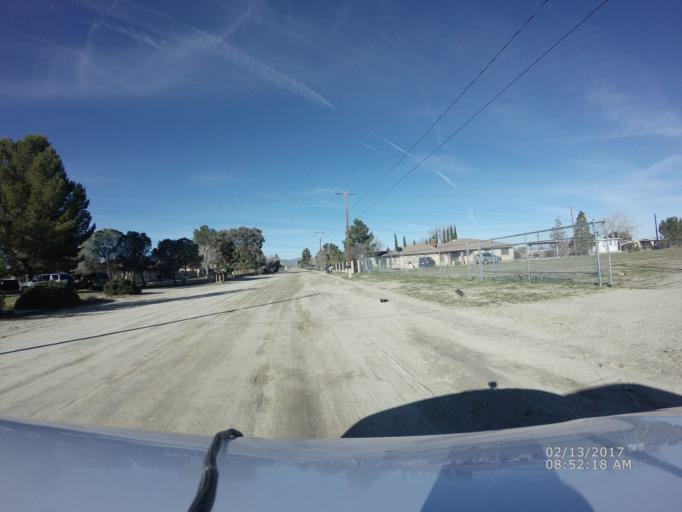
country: US
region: California
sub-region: Los Angeles County
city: Littlerock
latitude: 34.5412
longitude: -117.9688
